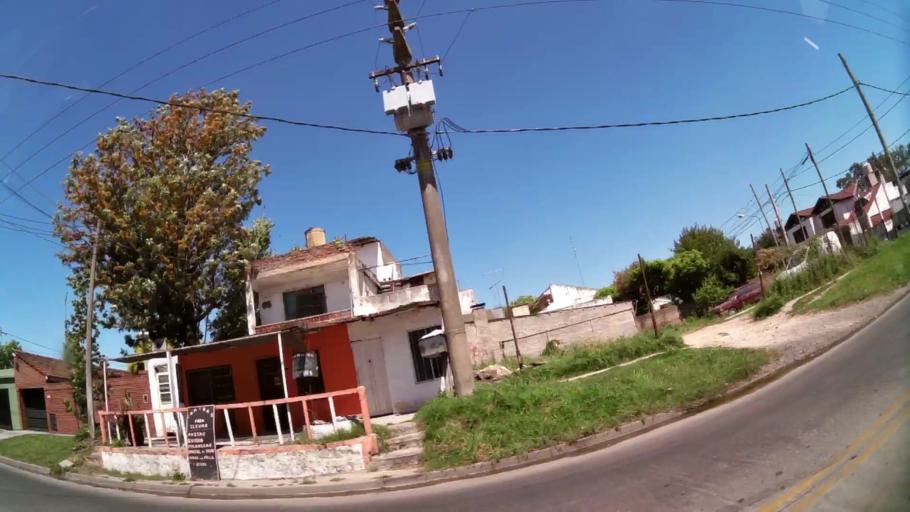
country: AR
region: Buenos Aires
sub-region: Partido de Tigre
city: Tigre
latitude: -34.4860
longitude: -58.6433
